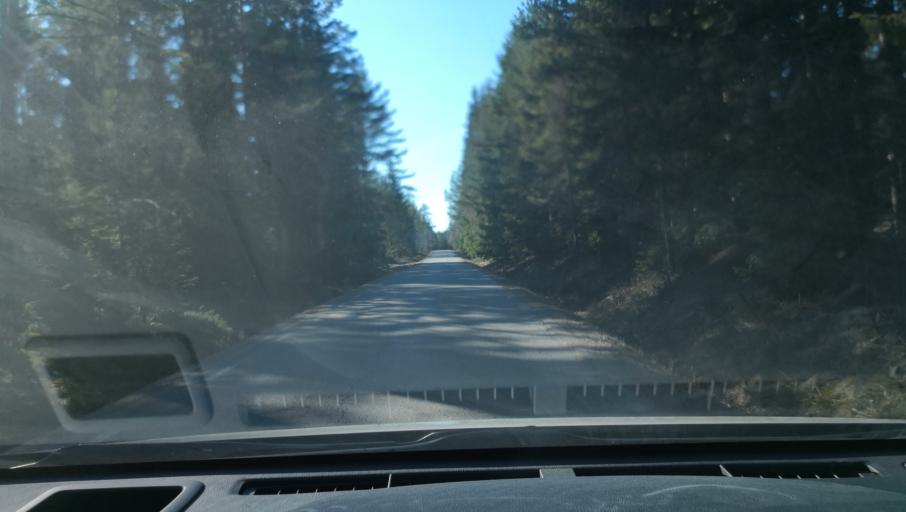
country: SE
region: Dalarna
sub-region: Avesta Kommun
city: Horndal
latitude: 60.0848
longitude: 16.4248
